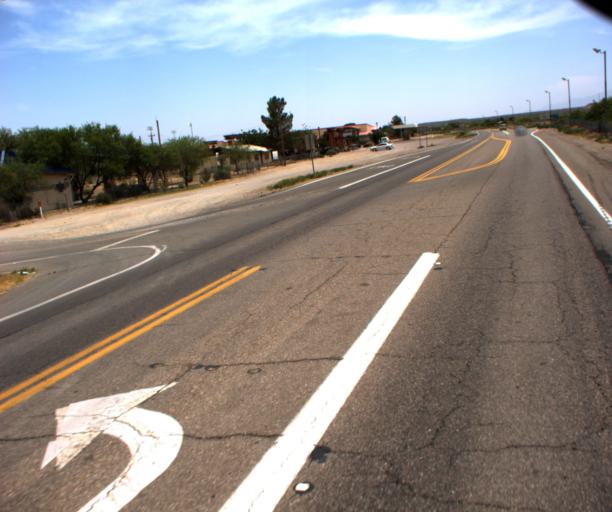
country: US
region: Arizona
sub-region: Graham County
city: Bylas
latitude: 33.1208
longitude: -110.1112
